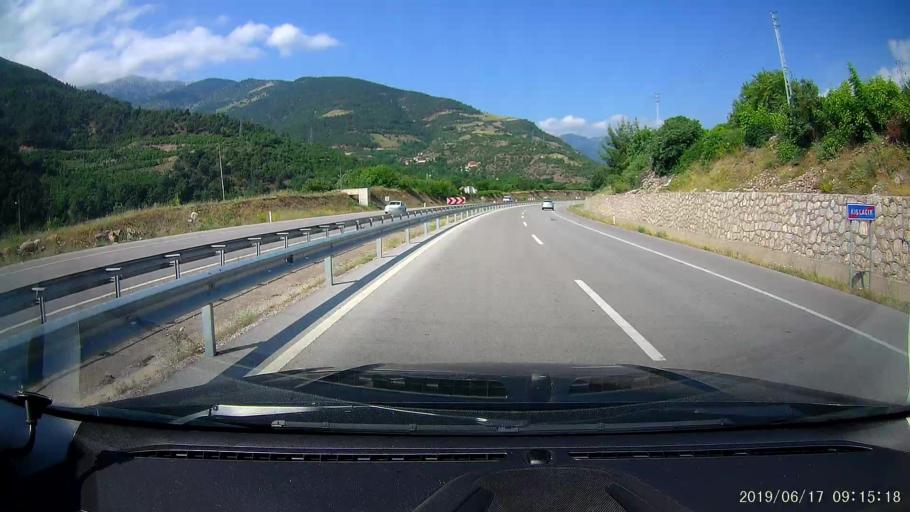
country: TR
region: Amasya
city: Akdag
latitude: 40.7474
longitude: 36.0405
